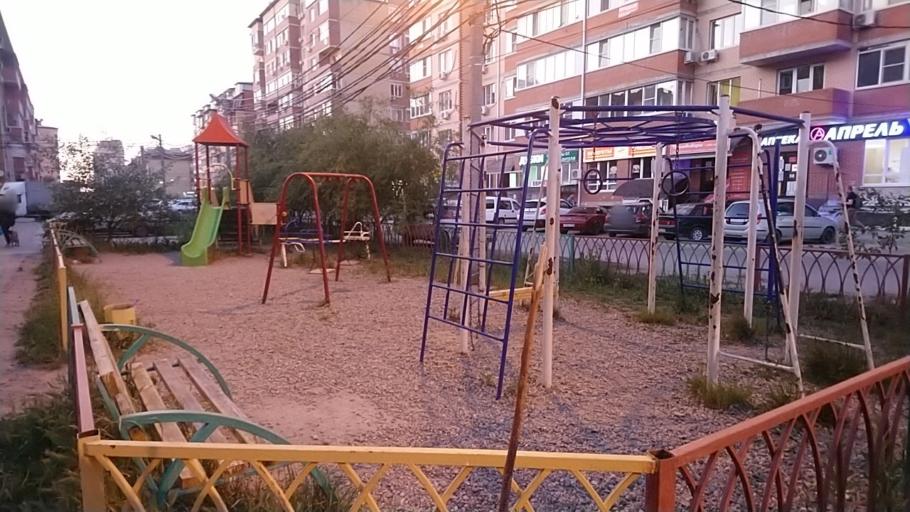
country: RU
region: Krasnodarskiy
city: Krasnodar
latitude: 45.0874
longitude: 39.0072
